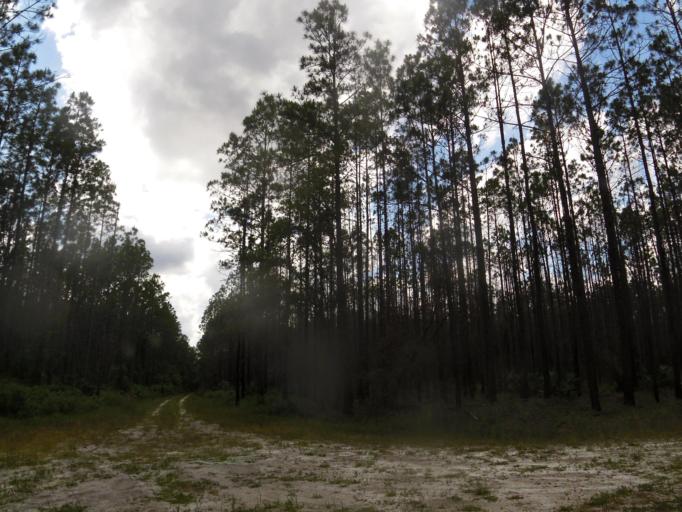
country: US
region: Florida
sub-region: Clay County
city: Keystone Heights
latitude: 29.8529
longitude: -81.8535
